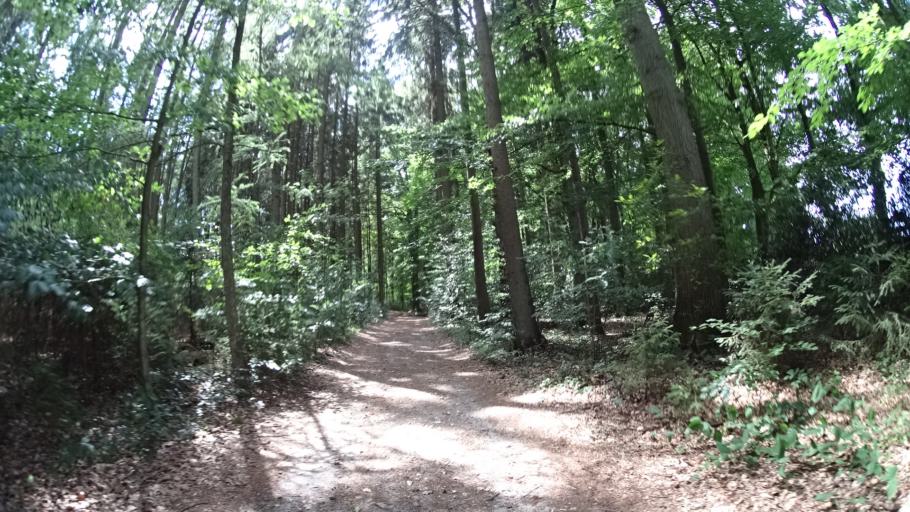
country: DE
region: Lower Saxony
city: Undeloh
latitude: 53.2310
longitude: 9.9216
